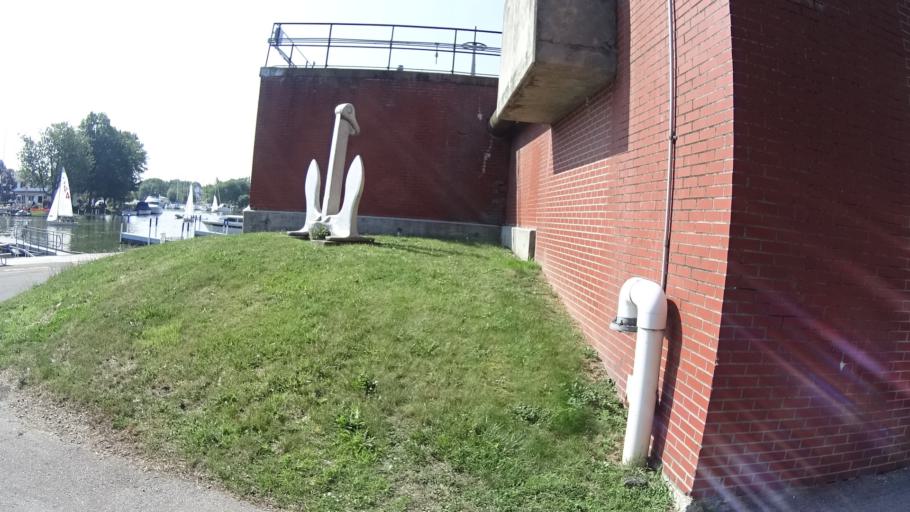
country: US
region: Ohio
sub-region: Lorain County
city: Vermilion
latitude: 41.4243
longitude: -82.3654
